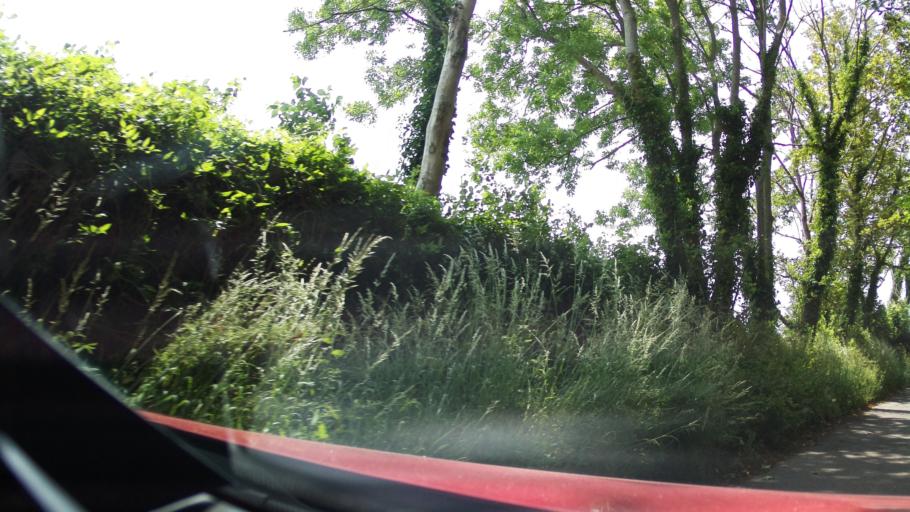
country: GB
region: Wales
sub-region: Vale of Glamorgan
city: Llantwit Major
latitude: 51.4036
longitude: -3.5168
